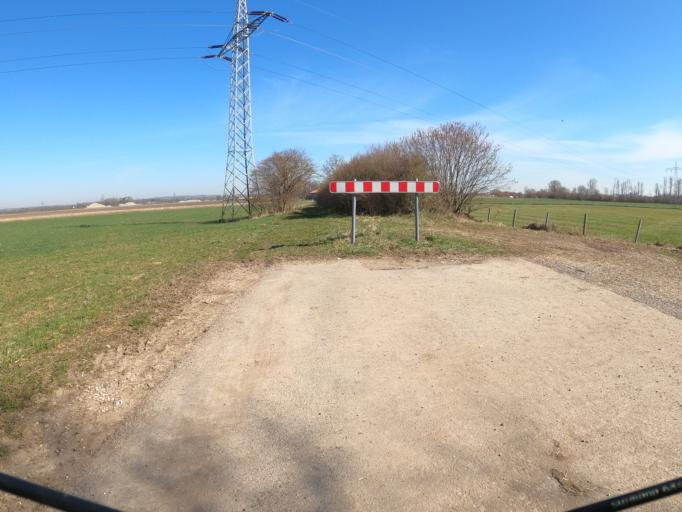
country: DE
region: Bavaria
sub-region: Swabia
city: Nersingen
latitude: 48.4529
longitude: 10.1525
